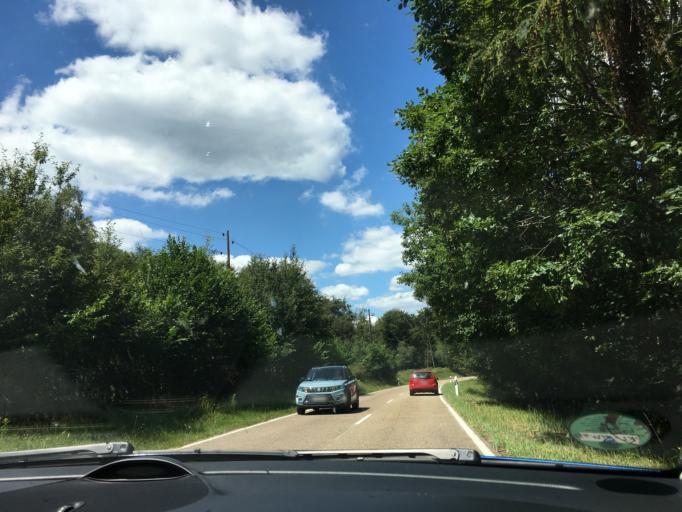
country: DE
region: Rheinland-Pfalz
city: Hauenstein
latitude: 49.2355
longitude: 7.8358
